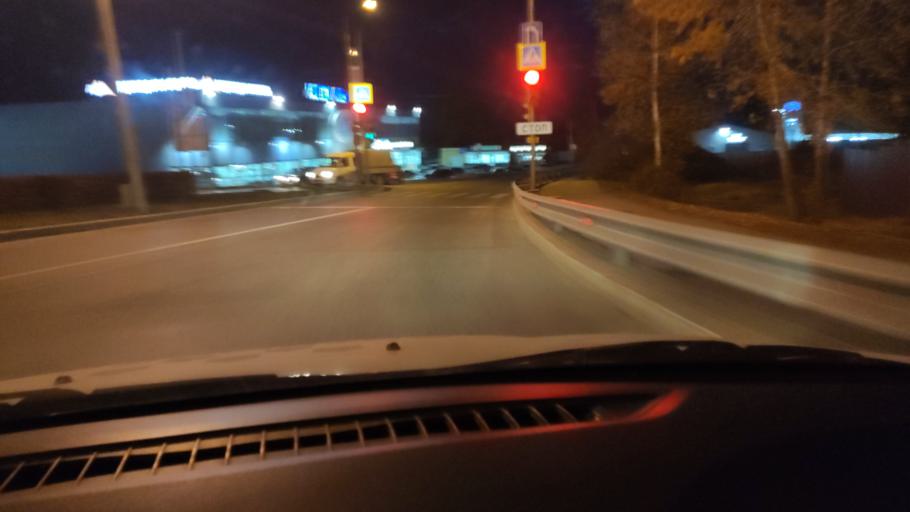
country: RU
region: Perm
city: Kondratovo
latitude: 57.9627
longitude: 56.1304
